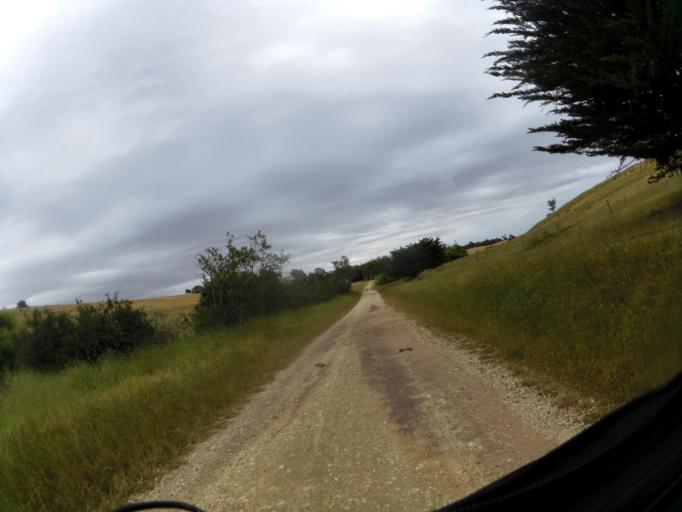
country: AU
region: Victoria
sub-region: Mount Alexander
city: Castlemaine
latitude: -37.2024
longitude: 144.0171
